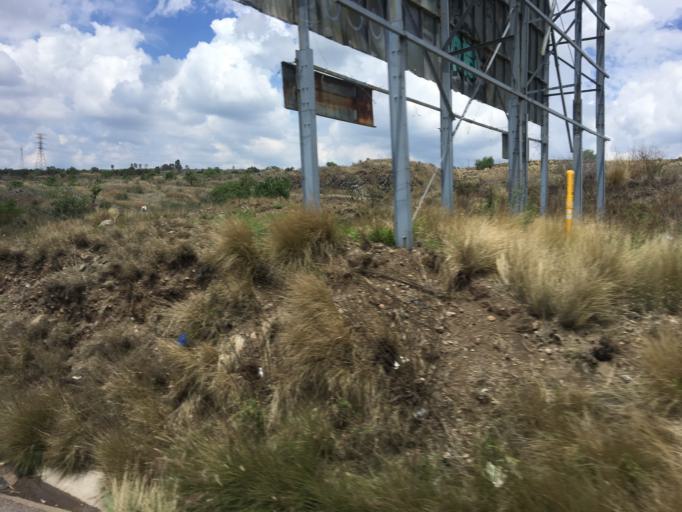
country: MX
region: Guanajuato
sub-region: Irapuato
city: Ex-Hacienda del Copal
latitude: 20.7425
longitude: -101.3405
